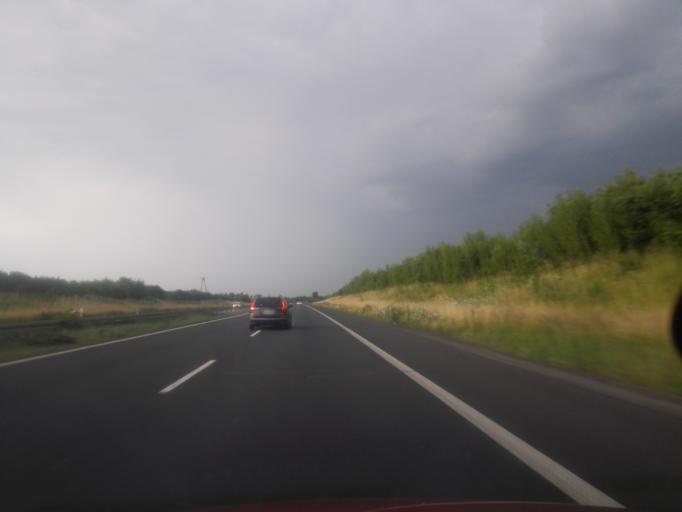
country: PL
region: Silesian Voivodeship
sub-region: Powiat czestochowski
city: Mykanow
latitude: 50.9309
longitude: 19.2296
